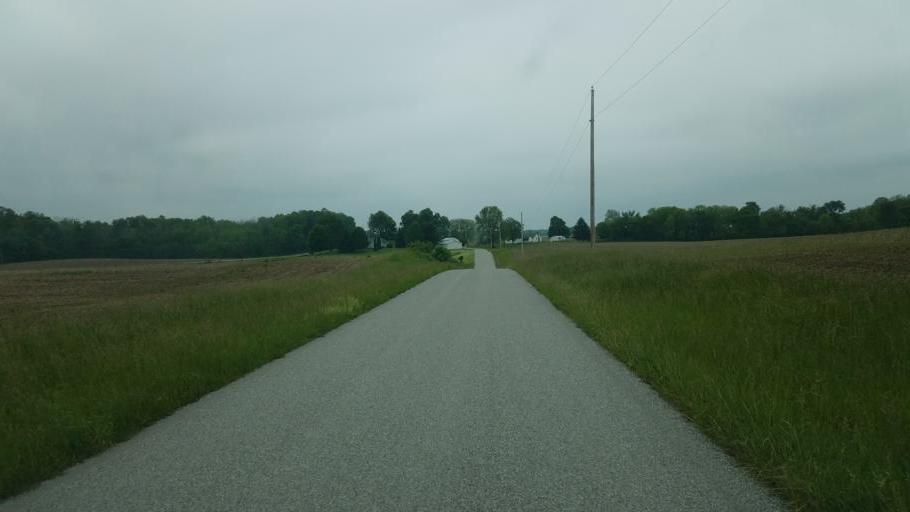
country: US
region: Ohio
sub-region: Knox County
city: Centerburg
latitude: 40.3770
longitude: -82.7364
